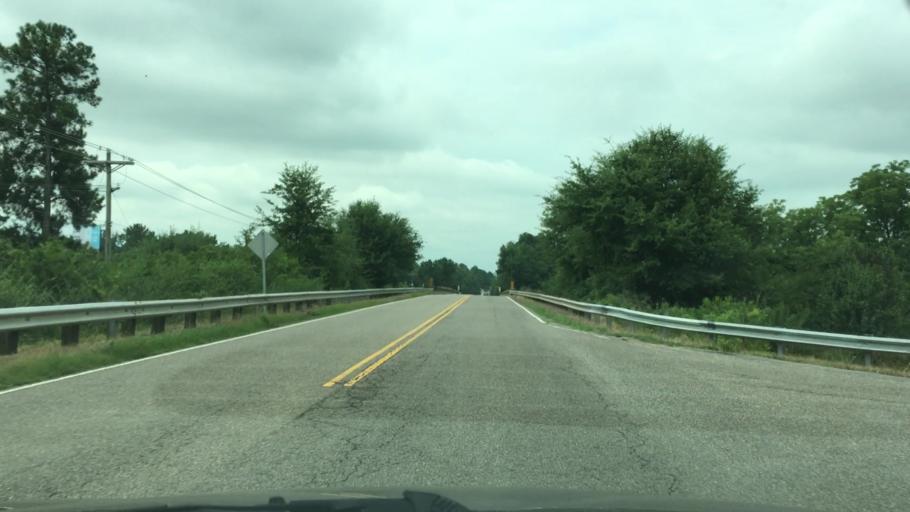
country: US
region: South Carolina
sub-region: Aiken County
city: Belvedere
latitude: 33.5502
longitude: -81.9576
